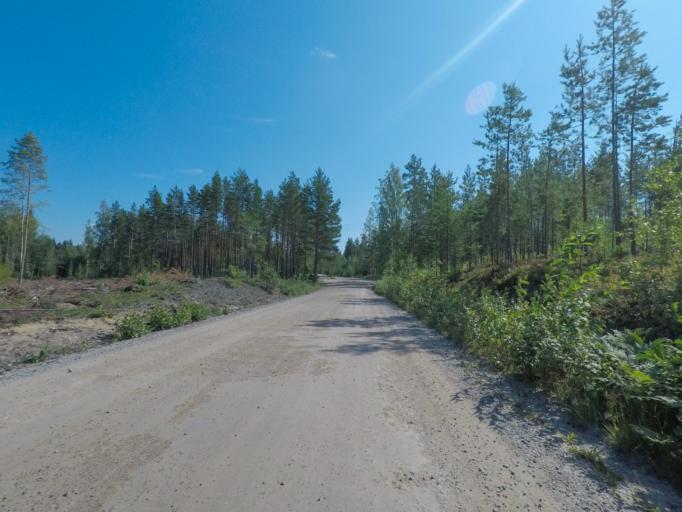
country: FI
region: Southern Savonia
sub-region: Mikkeli
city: Puumala
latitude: 61.4059
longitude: 28.0469
